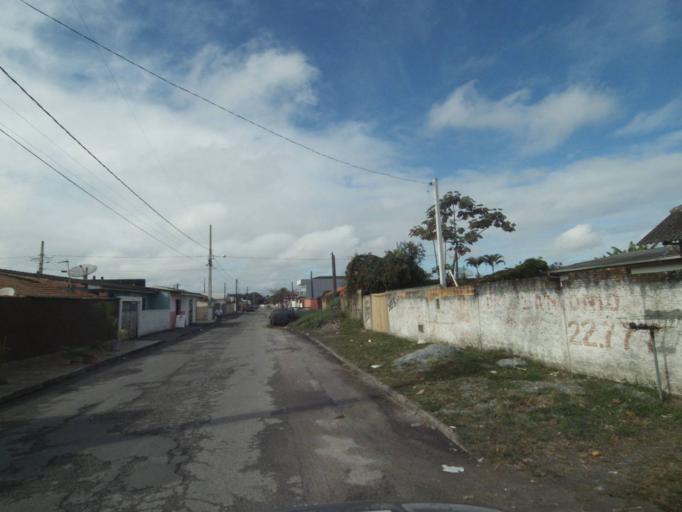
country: BR
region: Parana
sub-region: Paranagua
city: Paranagua
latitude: -25.5654
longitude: -48.5610
